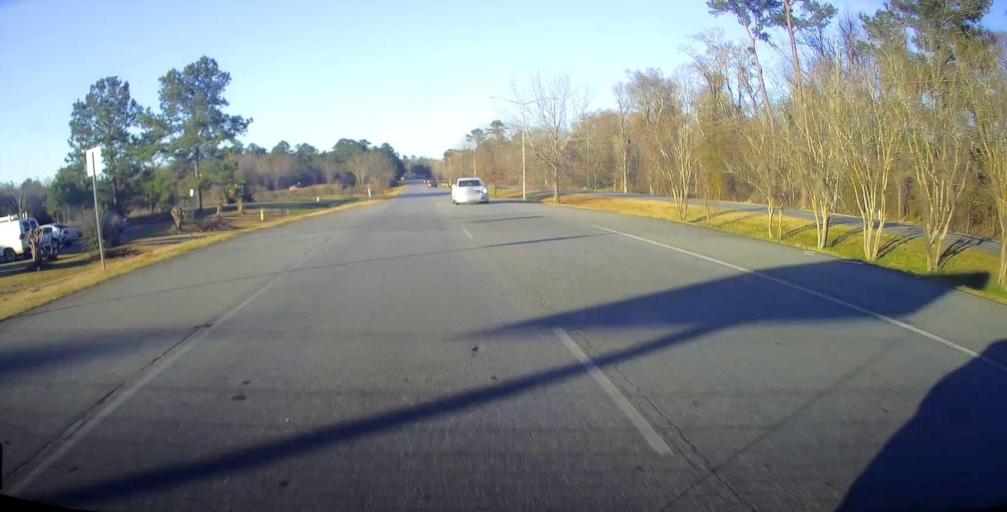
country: US
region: Georgia
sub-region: Dougherty County
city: Albany
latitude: 31.5733
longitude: -84.2209
